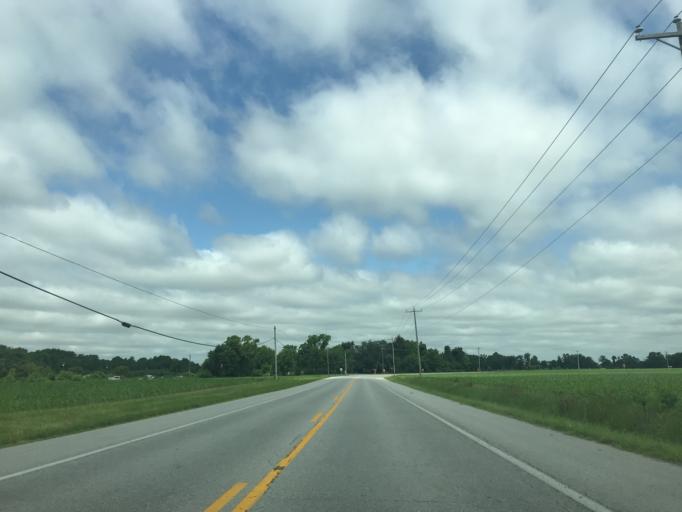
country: US
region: Maryland
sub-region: Caroline County
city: Ridgely
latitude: 38.9580
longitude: -75.8892
